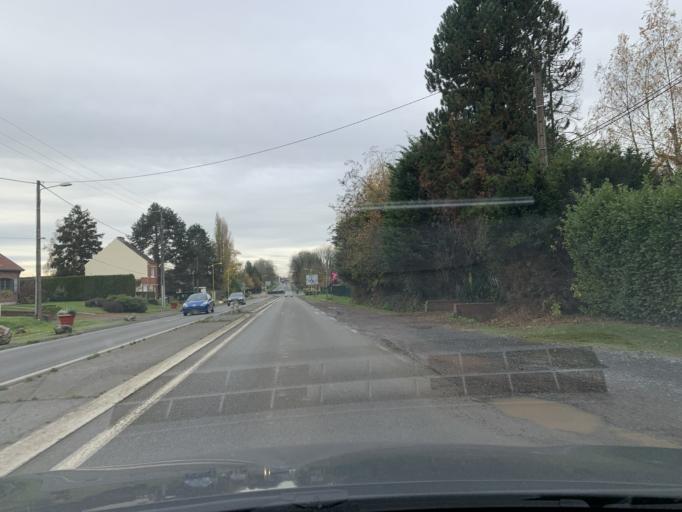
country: FR
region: Nord-Pas-de-Calais
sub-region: Departement du Nord
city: Aubigny-au-Bac
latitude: 50.2649
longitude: 3.1606
